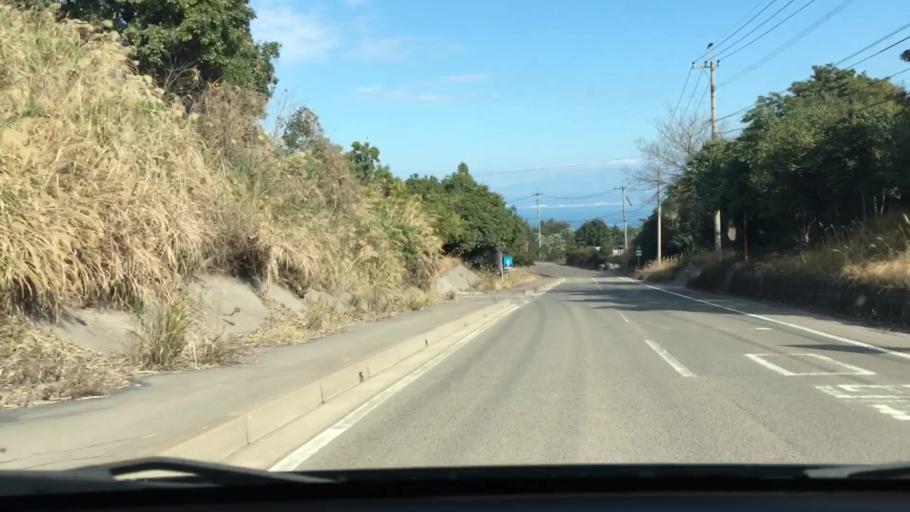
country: JP
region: Kagoshima
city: Hamanoichi
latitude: 31.6099
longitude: 130.7065
